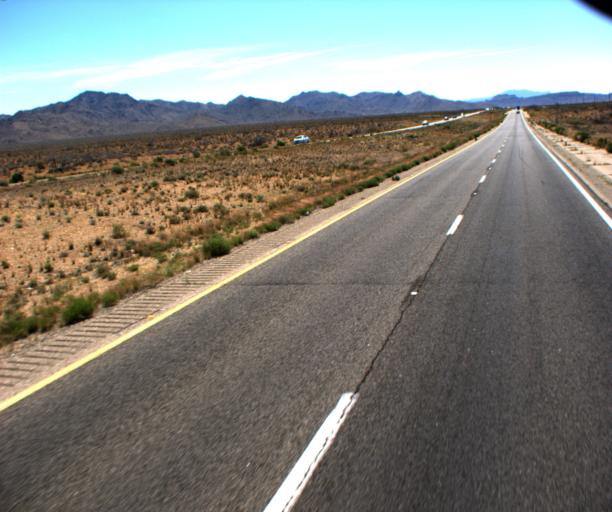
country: US
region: Arizona
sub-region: Mohave County
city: Golden Valley
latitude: 35.3074
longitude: -114.1948
